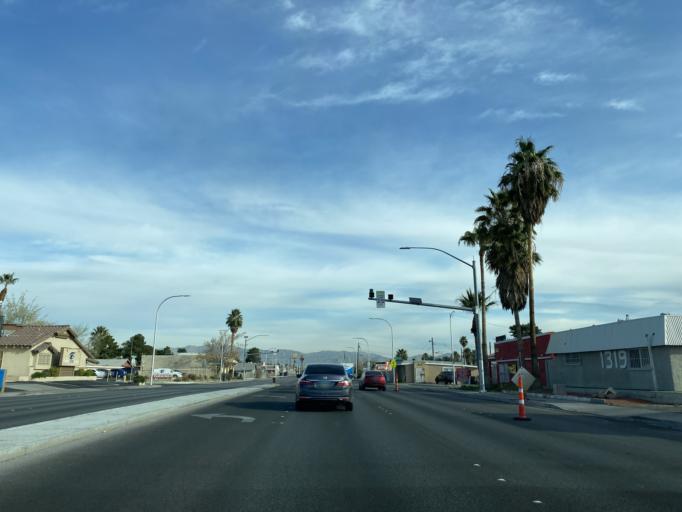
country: US
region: Nevada
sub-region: Clark County
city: Winchester
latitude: 36.1537
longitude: -115.1188
